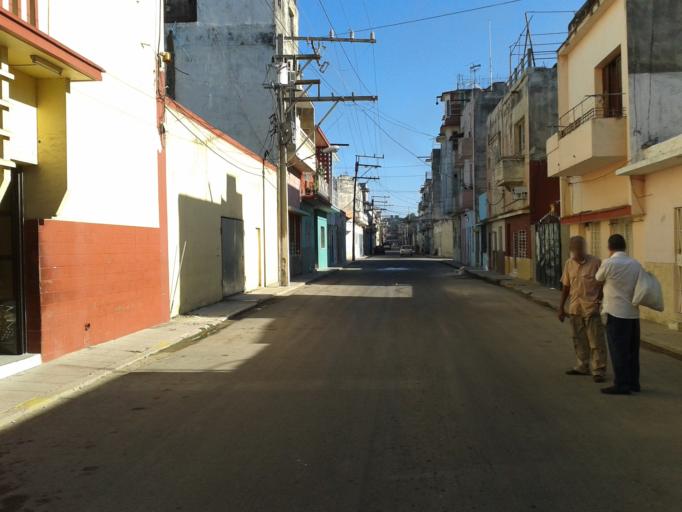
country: CU
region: La Habana
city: Havana
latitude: 23.1247
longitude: -82.3724
